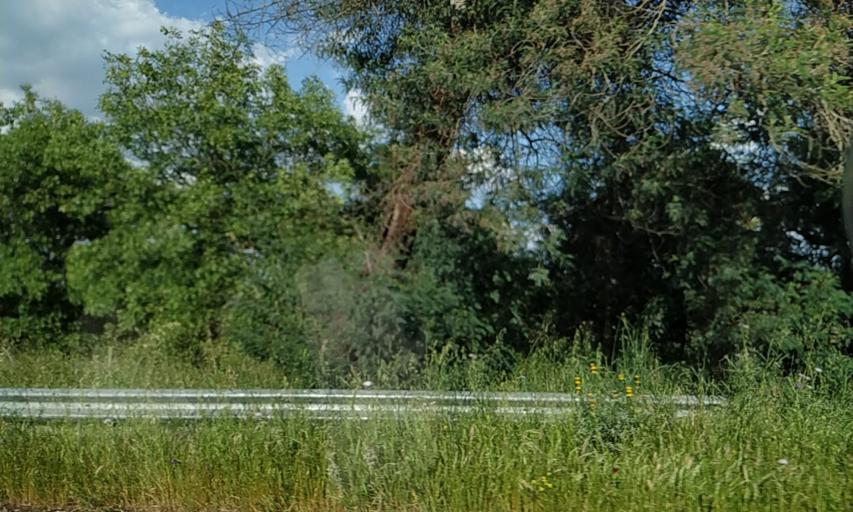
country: PT
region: Portalegre
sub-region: Portalegre
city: Urra
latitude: 39.1566
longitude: -7.4542
